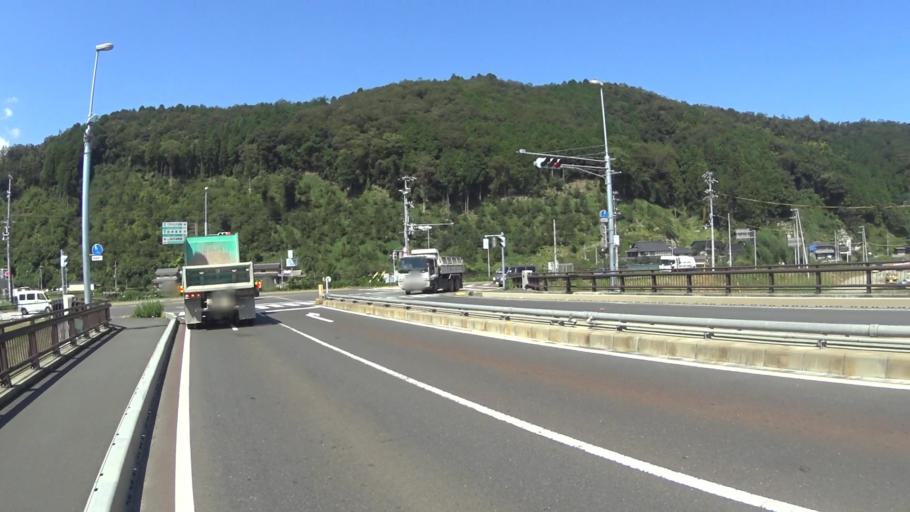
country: JP
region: Kyoto
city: Maizuru
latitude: 35.4529
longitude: 135.2661
